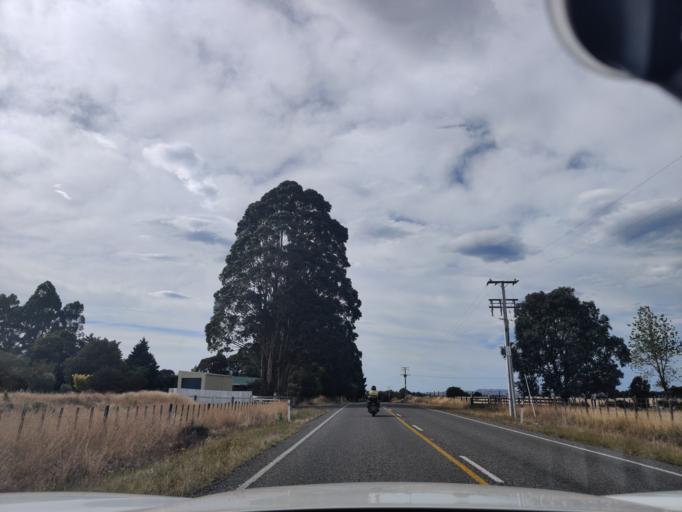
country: NZ
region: Wellington
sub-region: Masterton District
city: Masterton
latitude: -40.8749
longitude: 175.6521
